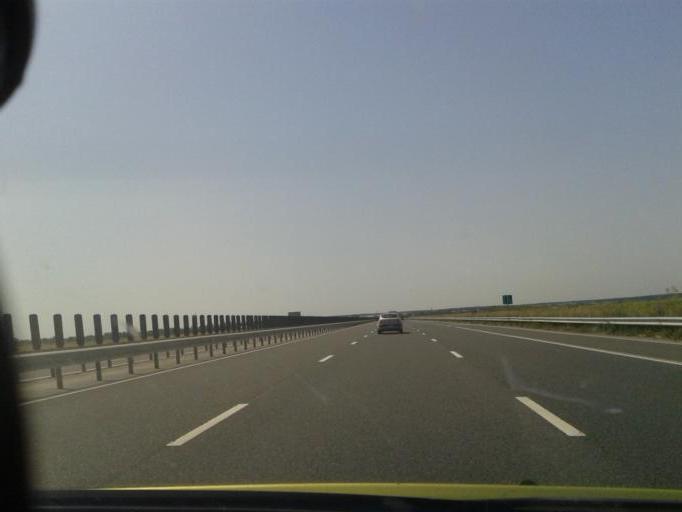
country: RO
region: Ilfov
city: Stefanestii de Jos
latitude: 44.5526
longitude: 26.1827
